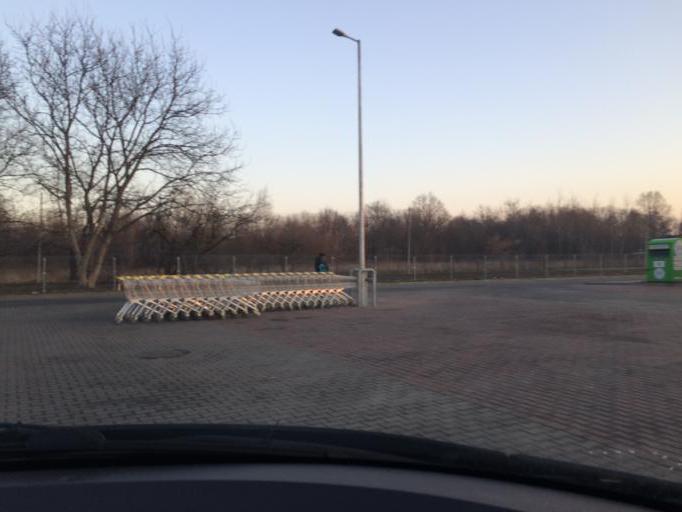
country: PL
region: Lesser Poland Voivodeship
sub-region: Powiat wielicki
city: Czarnochowice
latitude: 50.0230
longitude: 20.0420
